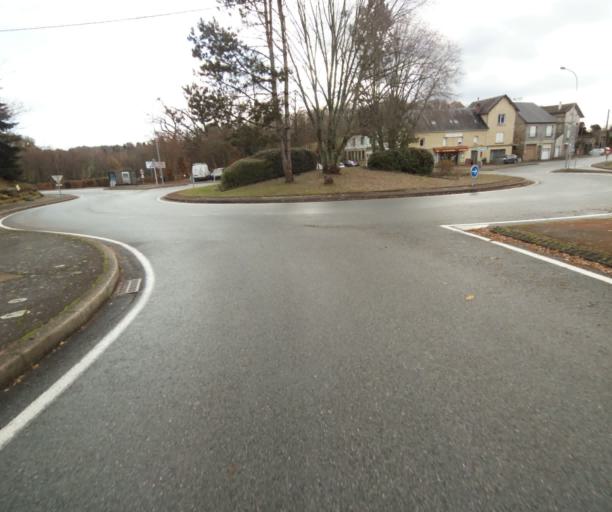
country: FR
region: Limousin
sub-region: Departement de la Correze
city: Saint-Mexant
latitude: 45.2649
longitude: 1.6391
